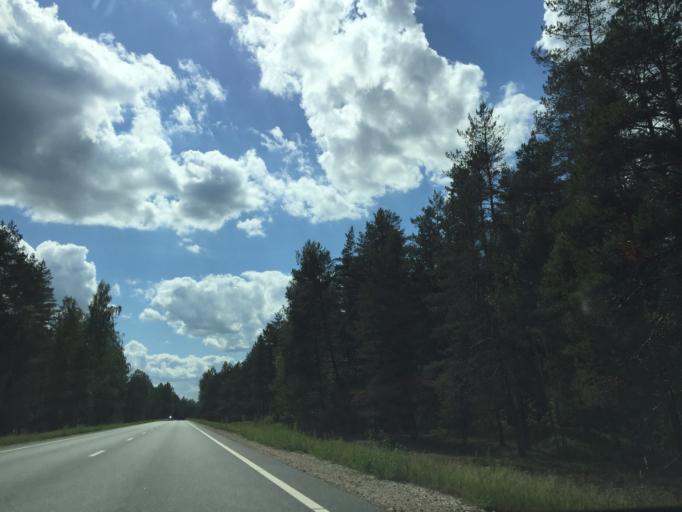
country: LV
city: Tireli
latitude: 56.7972
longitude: 23.4579
